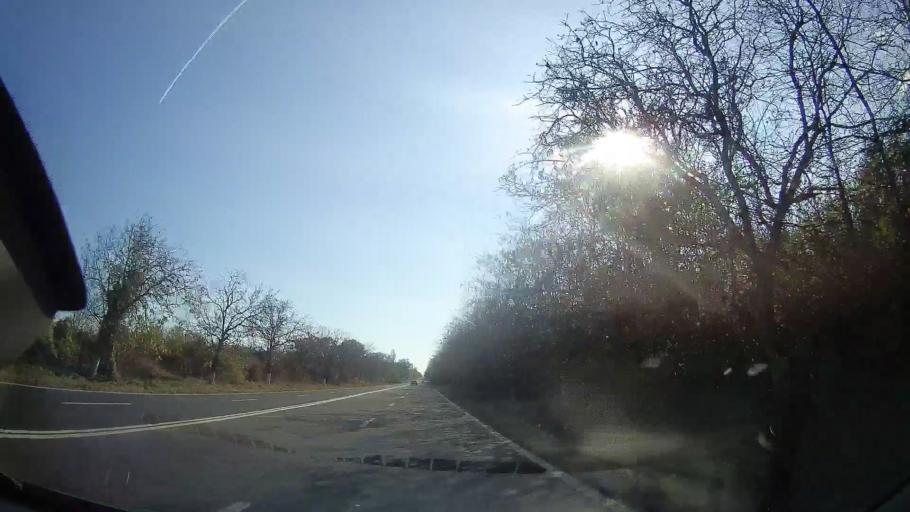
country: RO
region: Constanta
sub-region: Comuna Douazeci si Trei August
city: Dulcesti
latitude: 43.8794
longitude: 28.5736
